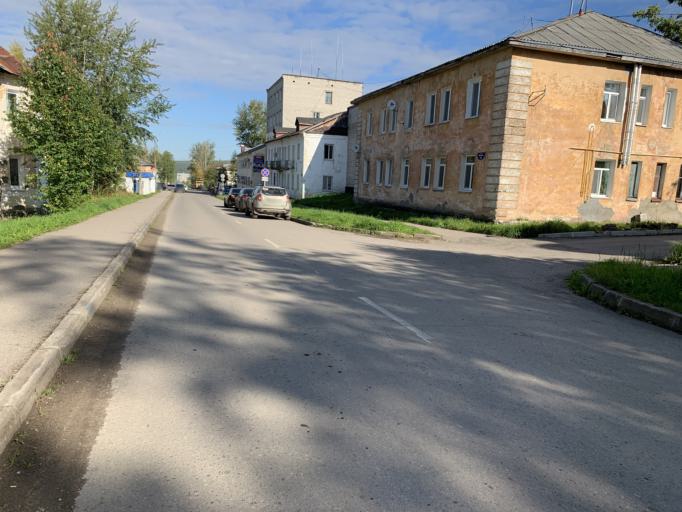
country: RU
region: Perm
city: Gubakha
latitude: 58.8411
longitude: 57.5546
